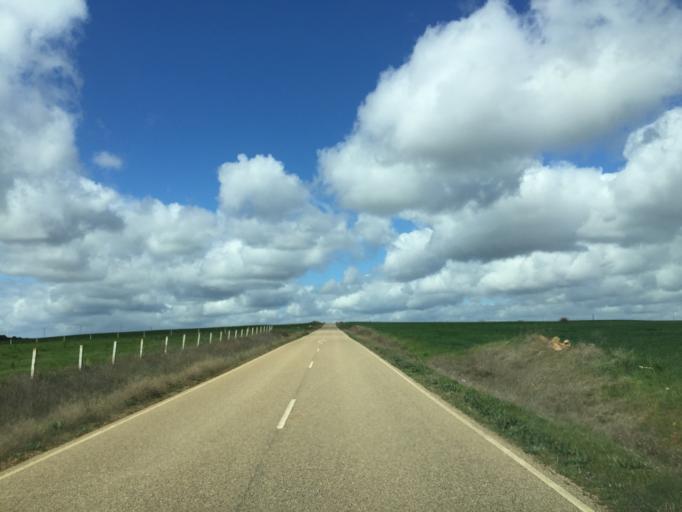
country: ES
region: Castille and Leon
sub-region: Provincia de Zamora
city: Manzanal del Barco
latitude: 41.5828
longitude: -5.9436
